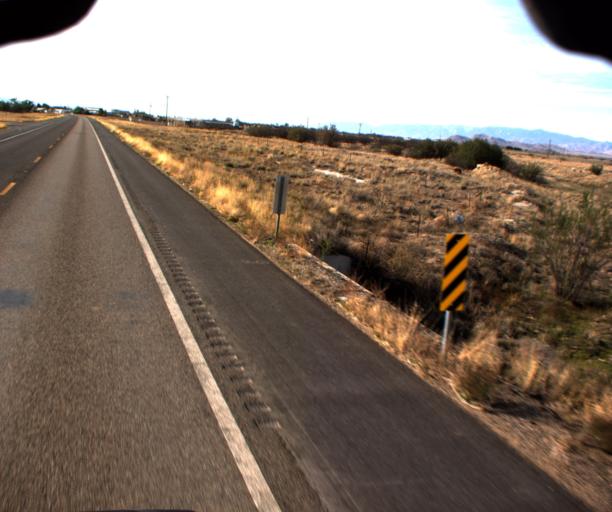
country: US
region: Arizona
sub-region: Cochise County
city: Willcox
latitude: 32.2419
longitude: -109.8146
